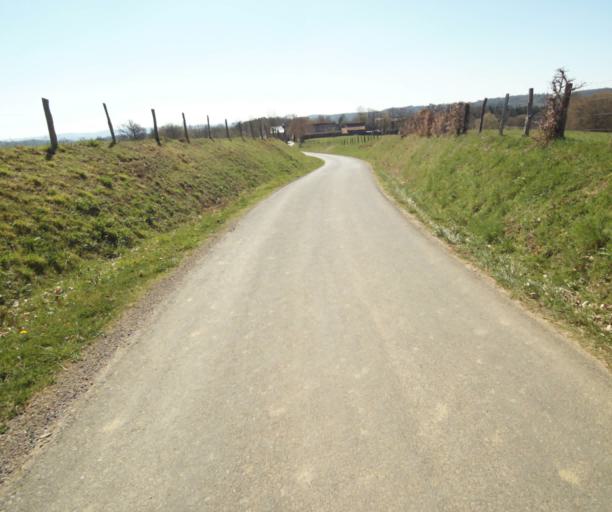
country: FR
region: Limousin
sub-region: Departement de la Correze
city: Saint-Clement
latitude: 45.3285
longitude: 1.7112
